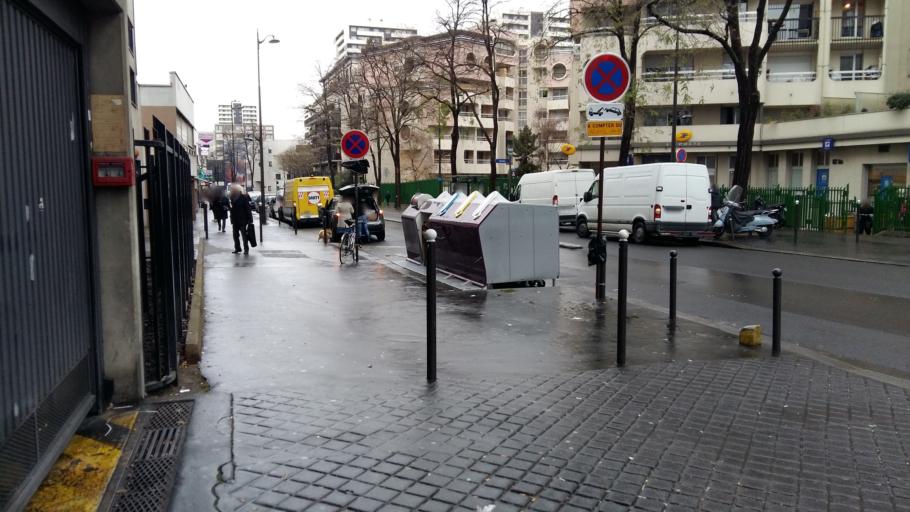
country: FR
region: Ile-de-France
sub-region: Departement de Seine-Saint-Denis
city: Aubervilliers
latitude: 48.8929
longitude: 2.3787
